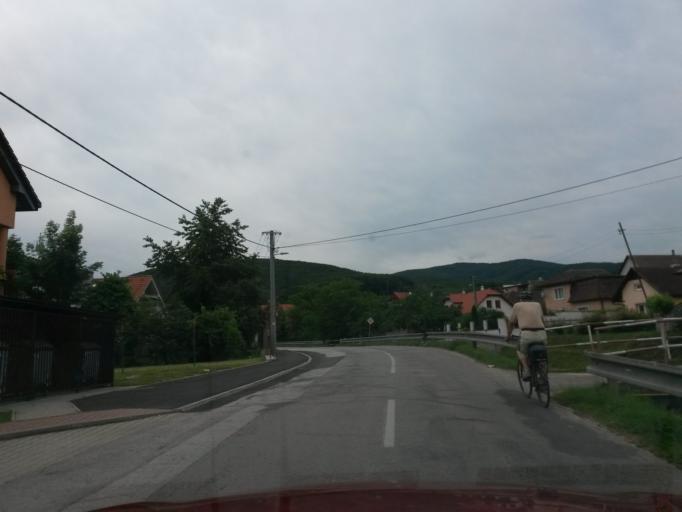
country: SK
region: Trenciansky
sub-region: Okres Trencin
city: Trencin
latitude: 48.8323
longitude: 18.0620
